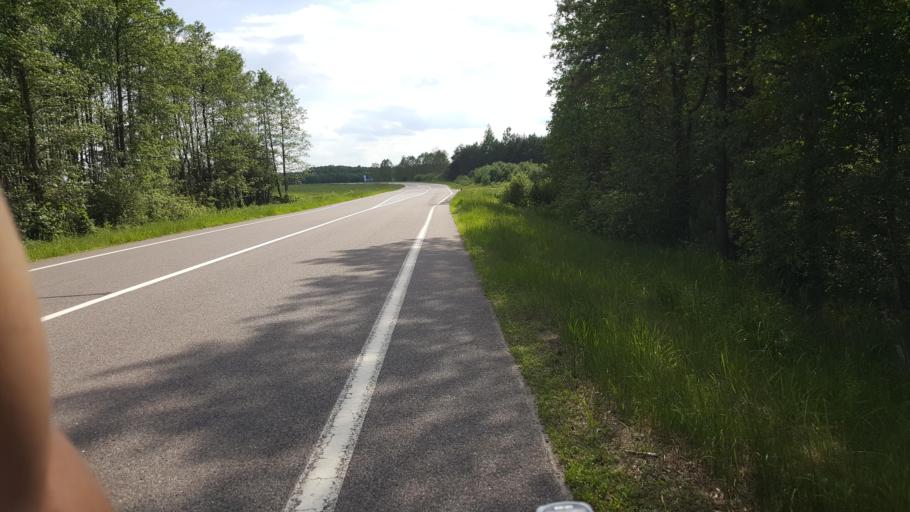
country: BY
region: Brest
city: Zhabinka
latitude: 52.4665
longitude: 24.1483
